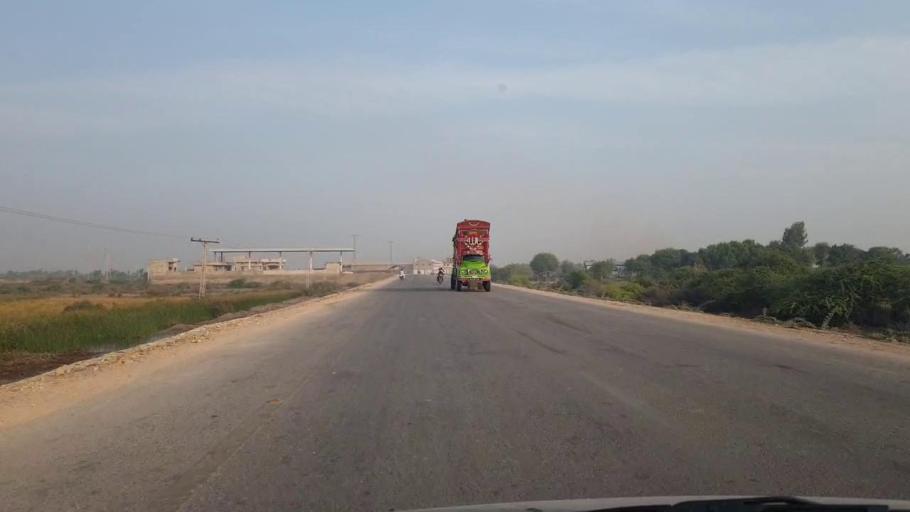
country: PK
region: Sindh
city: Badin
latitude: 24.6829
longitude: 68.8249
